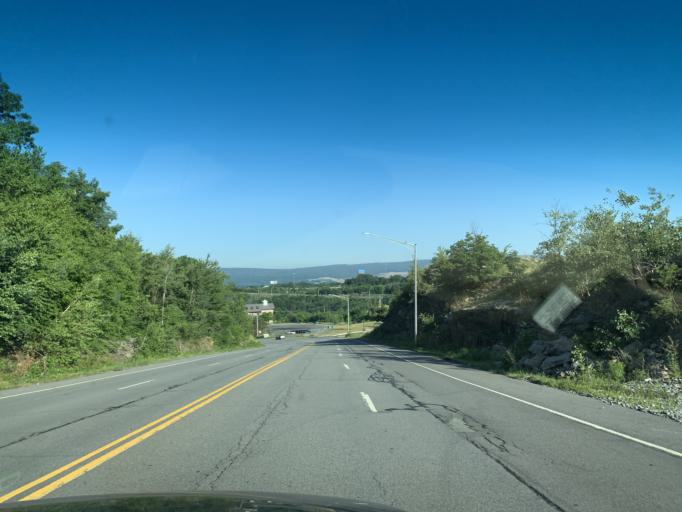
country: US
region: Pennsylvania
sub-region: Lackawanna County
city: Taylor
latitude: 41.3643
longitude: -75.6823
